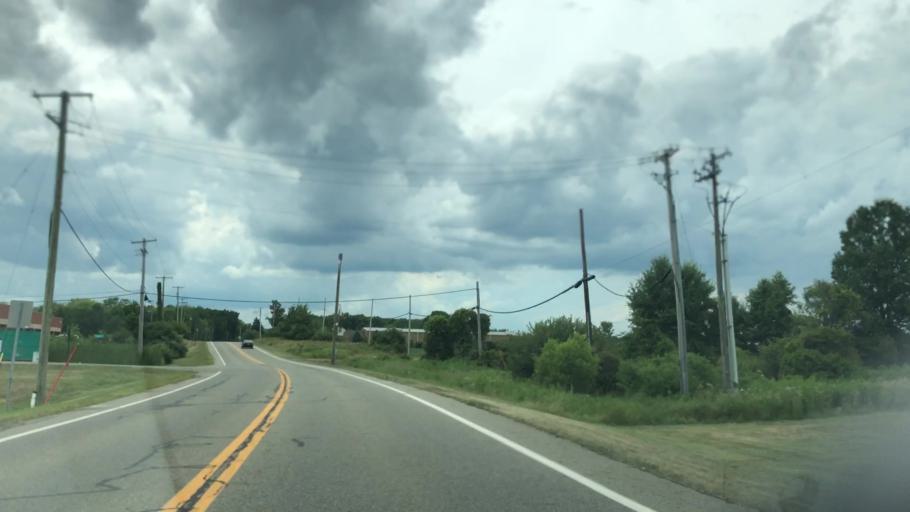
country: US
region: Ohio
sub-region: Summit County
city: Greensburg
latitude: 40.9301
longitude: -81.4433
